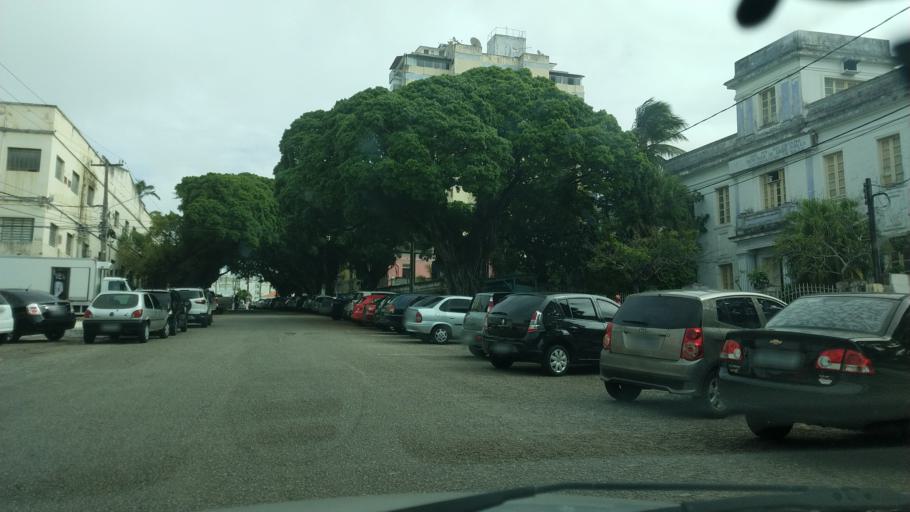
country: BR
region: Rio Grande do Norte
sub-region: Natal
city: Natal
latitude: -5.7831
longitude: -35.2073
